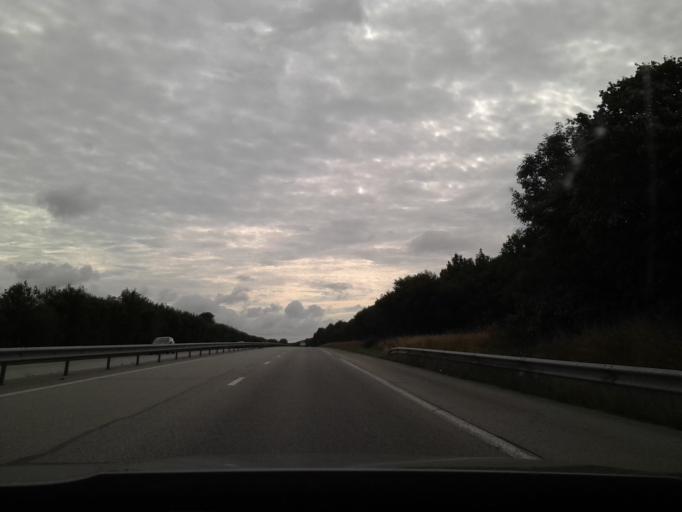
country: FR
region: Lower Normandy
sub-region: Departement du Calvados
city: Isigny-sur-Mer
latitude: 49.3082
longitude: -1.1248
